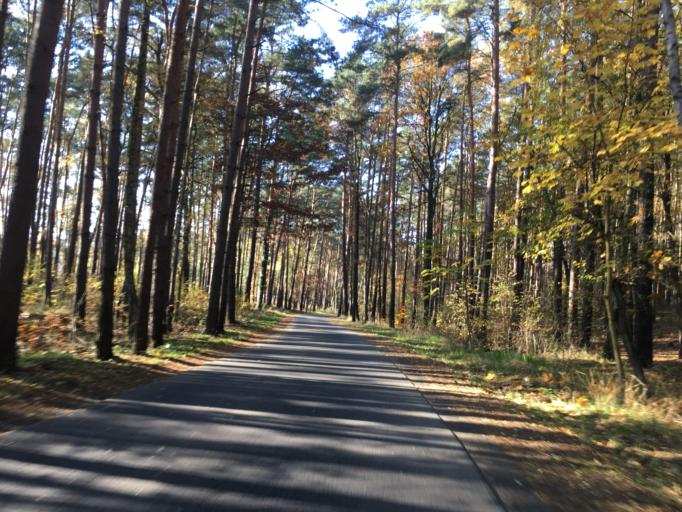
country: DE
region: Brandenburg
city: Reichenwalde
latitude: 52.2928
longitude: 14.0053
